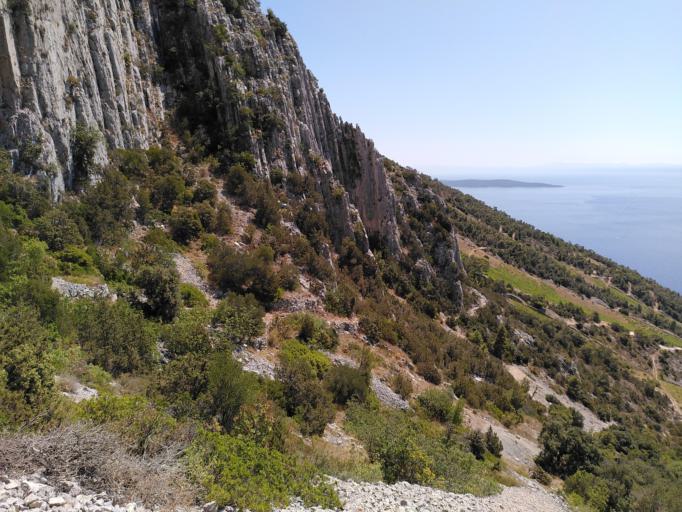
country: HR
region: Splitsko-Dalmatinska
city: Stari Grad
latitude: 43.1446
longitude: 16.5867
